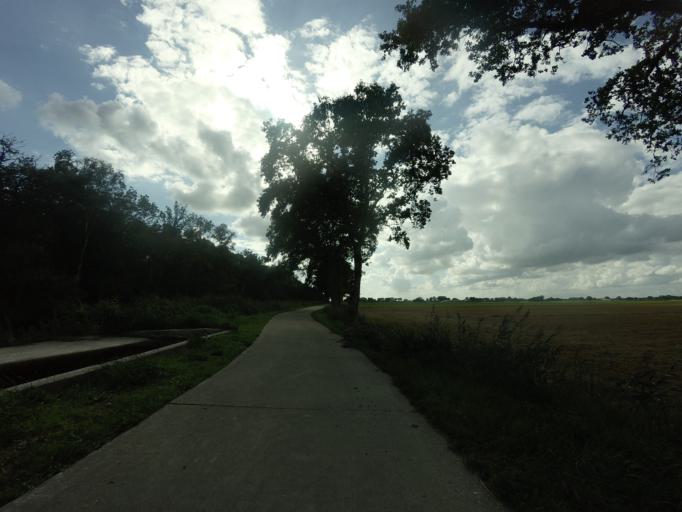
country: NL
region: Overijssel
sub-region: Gemeente Steenwijkerland
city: Giethoorn
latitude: 52.7344
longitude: 6.0265
